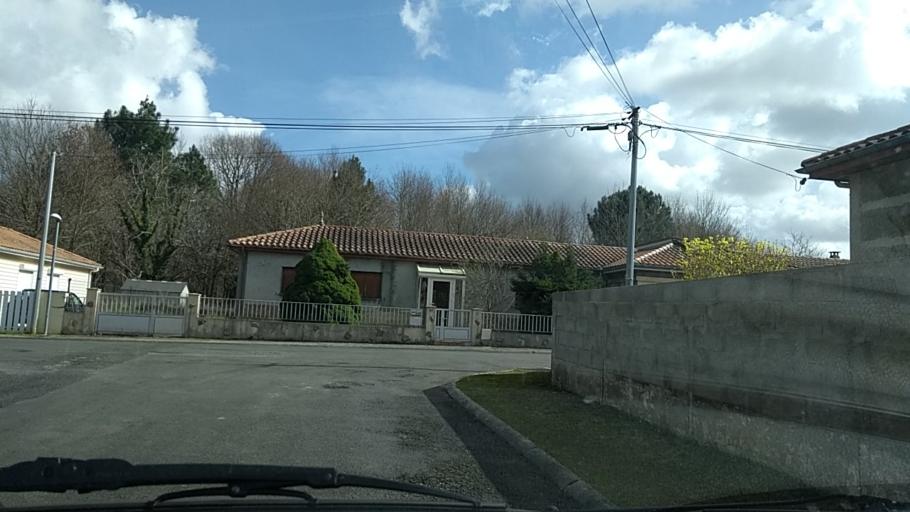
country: FR
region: Aquitaine
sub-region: Departement de la Gironde
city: Salles
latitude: 44.5529
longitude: -0.8655
